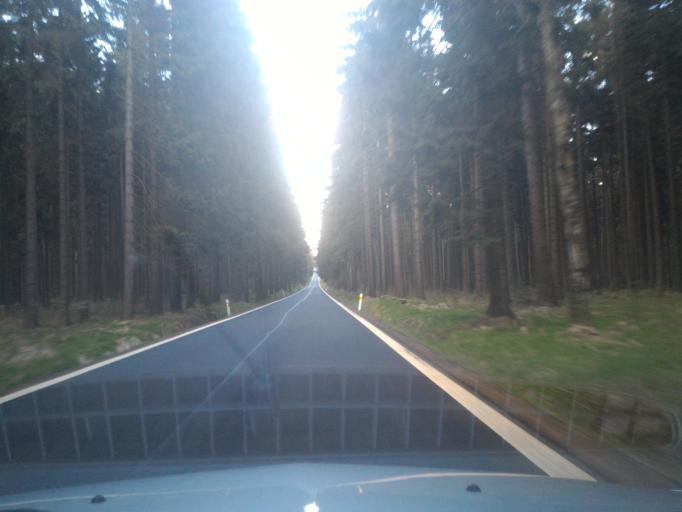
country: CZ
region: Ustecky
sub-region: Okres Decin
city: Krasna Lipa
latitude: 50.9063
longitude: 14.5473
